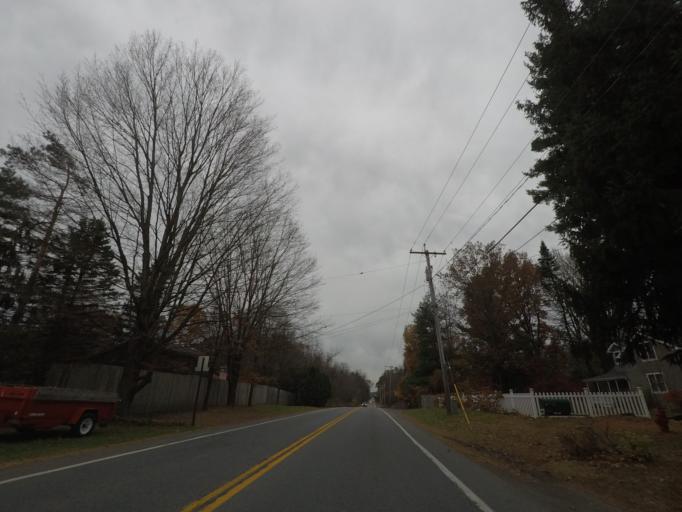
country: US
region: New York
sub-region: Saratoga County
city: Country Knolls
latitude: 42.8581
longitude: -73.8202
